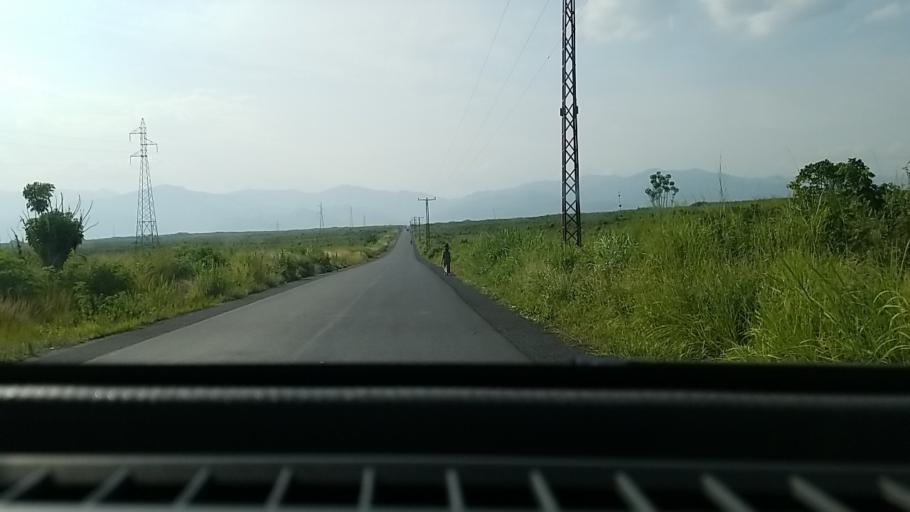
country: CD
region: Nord Kivu
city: Sake
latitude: -1.6000
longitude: 29.1147
